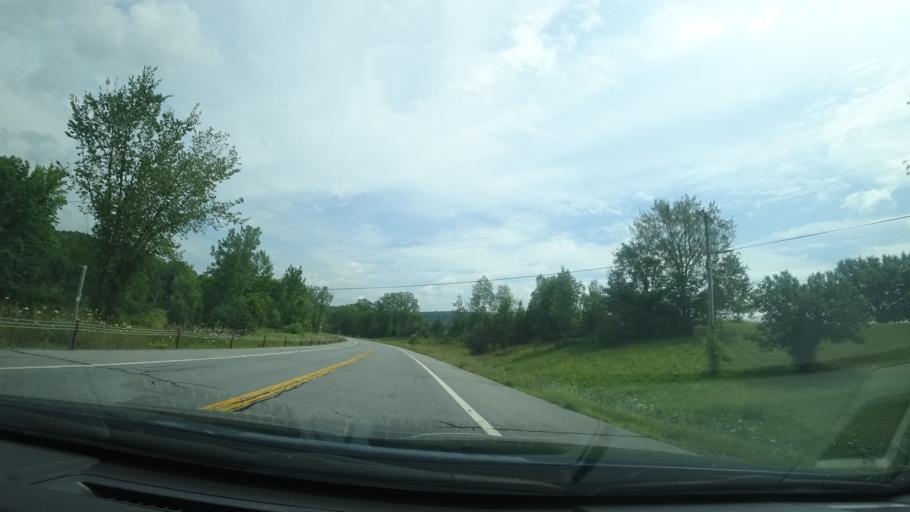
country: US
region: New York
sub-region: Washington County
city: Whitehall
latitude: 43.6628
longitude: -73.4233
